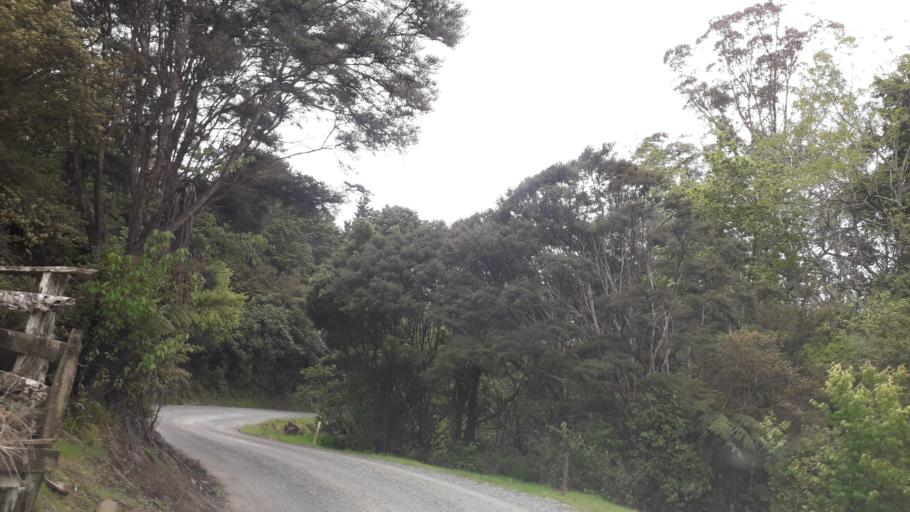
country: NZ
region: Northland
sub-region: Far North District
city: Taipa
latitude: -35.0690
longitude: 173.5536
